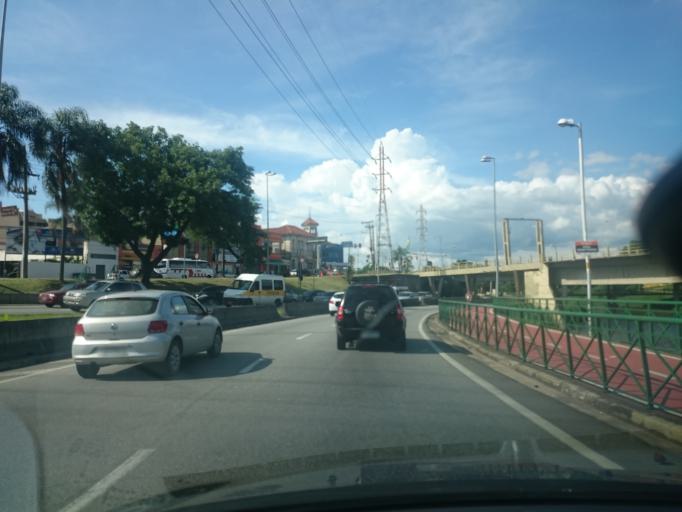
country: BR
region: Sao Paulo
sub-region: Sorocaba
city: Sorocaba
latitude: -23.5027
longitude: -47.4525
